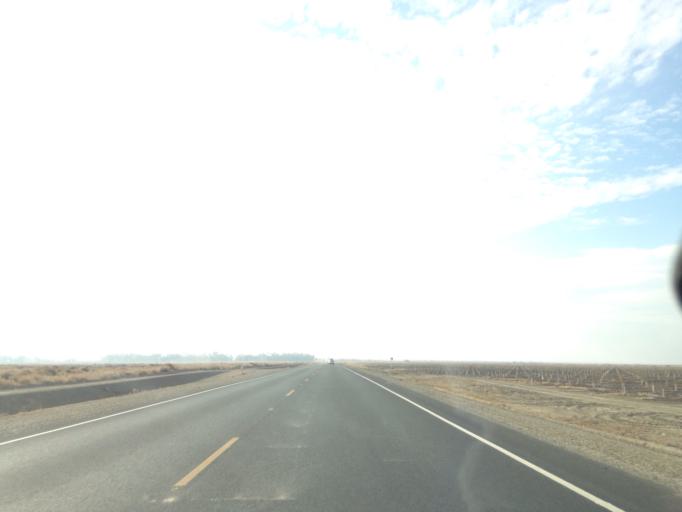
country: US
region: California
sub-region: Kern County
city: Lost Hills
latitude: 35.6162
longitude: -119.6290
